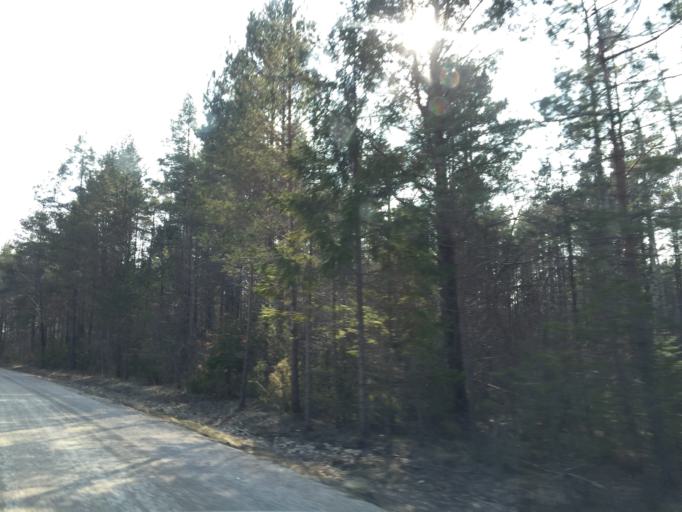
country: EE
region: Saare
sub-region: Orissaare vald
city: Orissaare
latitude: 58.5649
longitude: 23.2729
